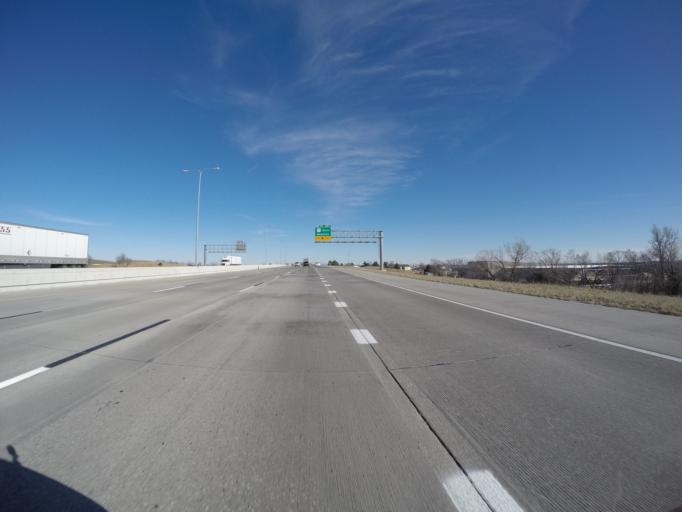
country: US
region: Nebraska
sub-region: Lancaster County
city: Lincoln
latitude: 40.8157
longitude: -96.7709
